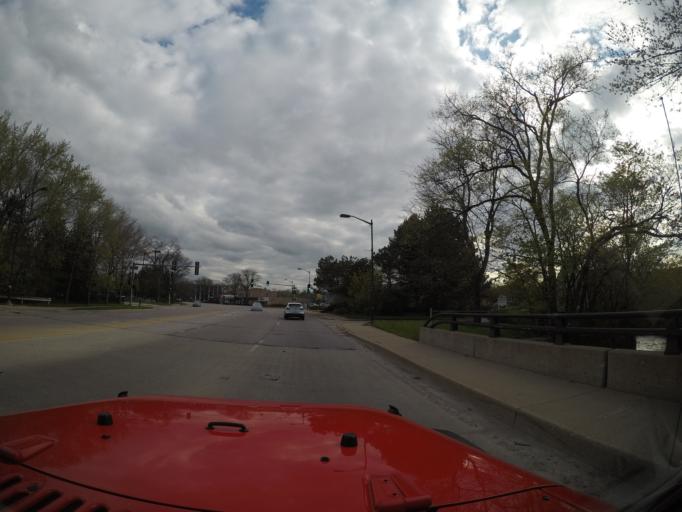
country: US
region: Illinois
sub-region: Cook County
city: Glenview
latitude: 42.0721
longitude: -87.7995
